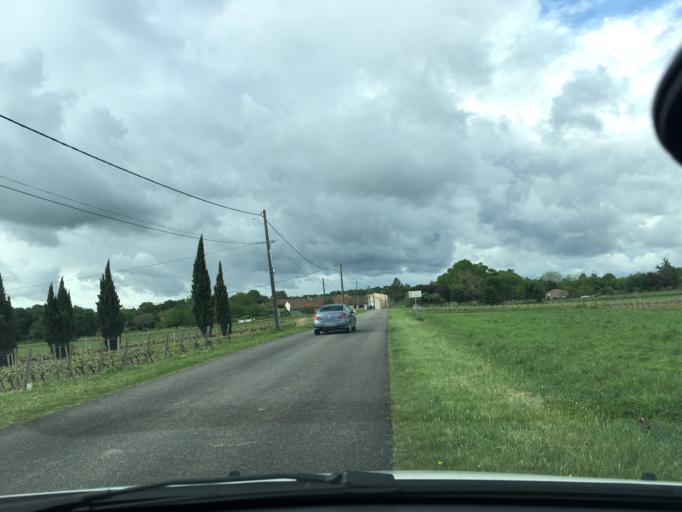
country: FR
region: Aquitaine
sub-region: Departement de la Gironde
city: Vertheuil
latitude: 45.3185
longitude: -0.8376
